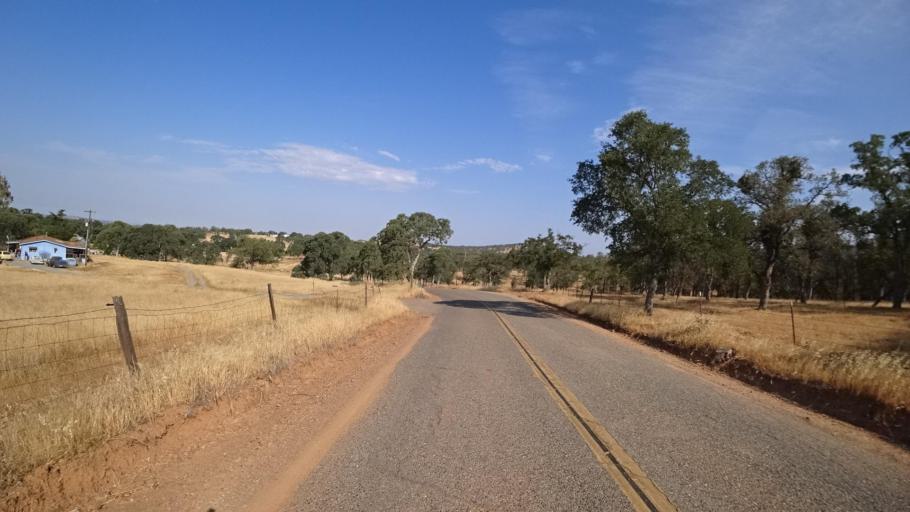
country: US
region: California
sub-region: Tuolumne County
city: Tuolumne City
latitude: 37.7033
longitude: -120.2929
